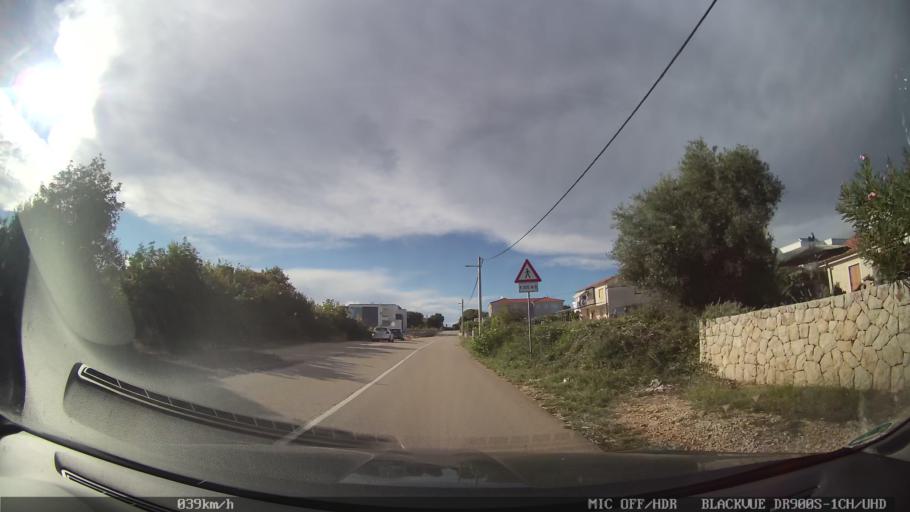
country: HR
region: Primorsko-Goranska
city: Njivice
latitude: 45.0707
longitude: 14.4678
